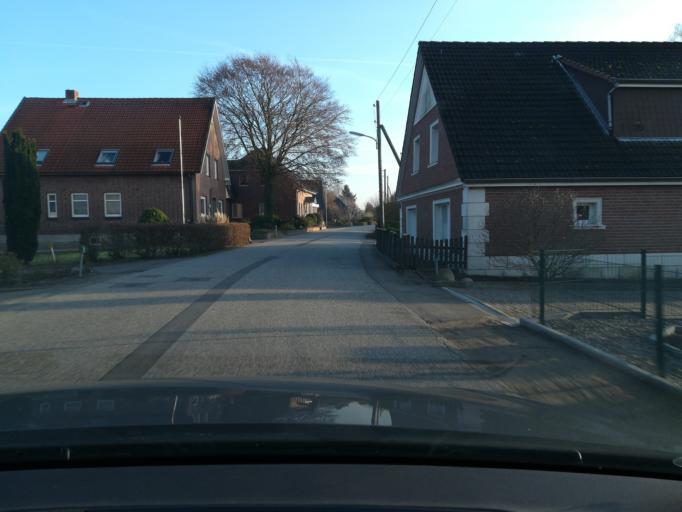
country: DE
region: Hamburg
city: Bergedorf
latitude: 53.4372
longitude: 10.1979
